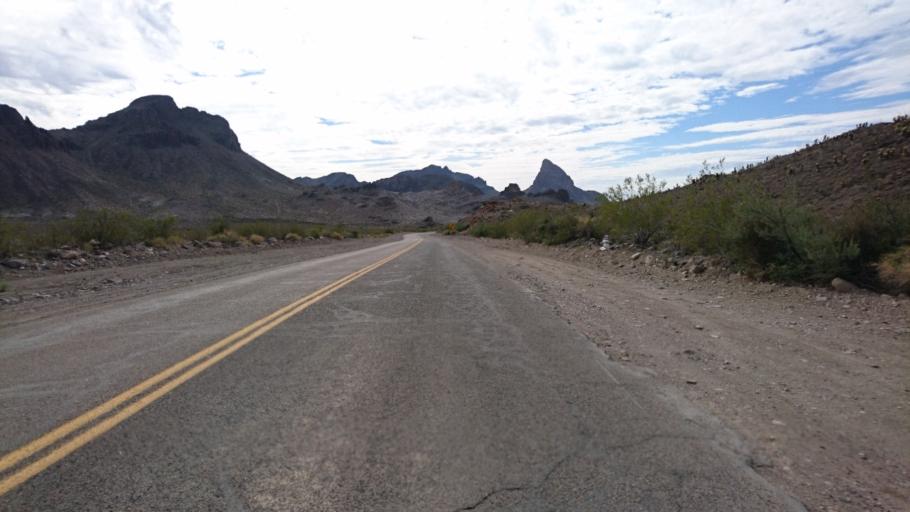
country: US
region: Arizona
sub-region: Mohave County
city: Mohave Valley
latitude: 35.0101
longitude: -114.3908
